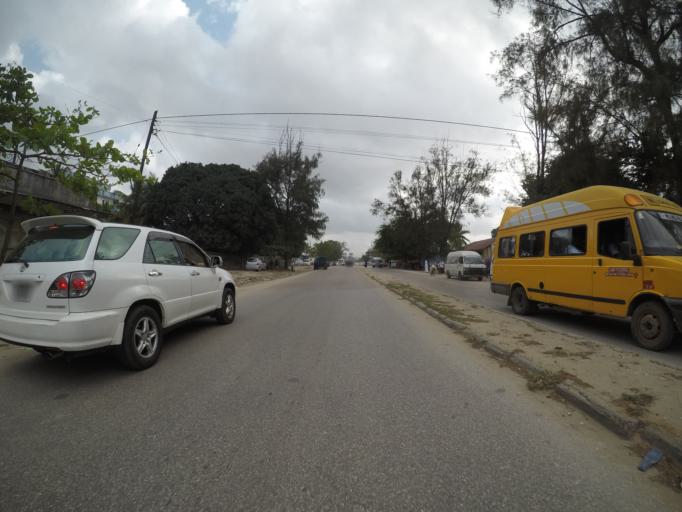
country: TZ
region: Zanzibar Urban/West
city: Zanzibar
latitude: -6.1783
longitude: 39.2220
